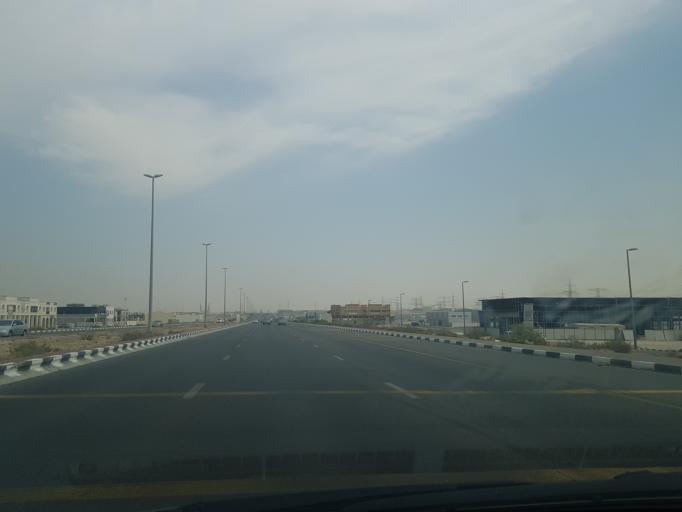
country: AE
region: Ash Shariqah
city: Sharjah
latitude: 25.2513
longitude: 55.5317
